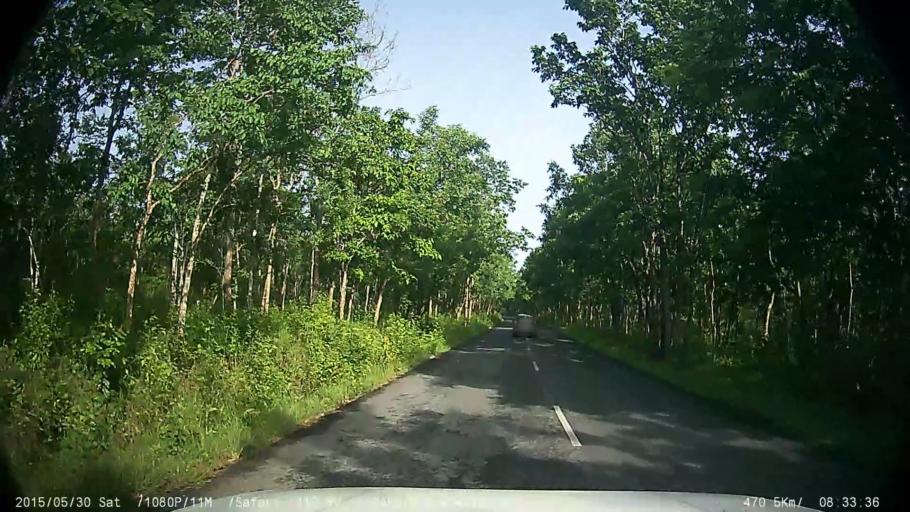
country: IN
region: Tamil Nadu
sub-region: Nilgiri
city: Masinigudi
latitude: 11.7282
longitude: 76.4470
